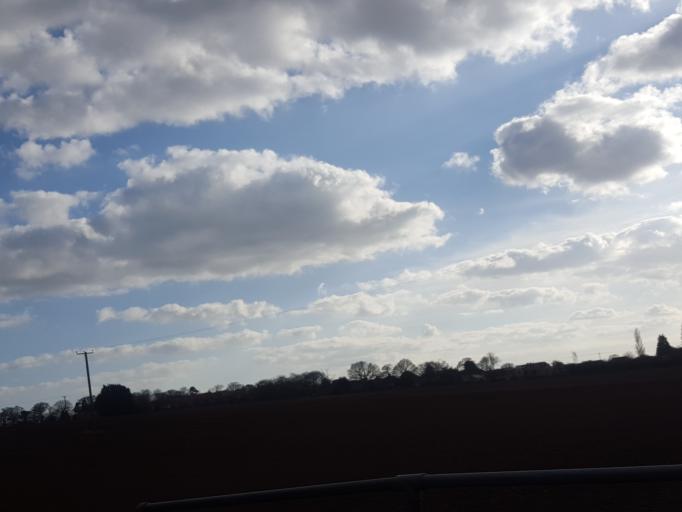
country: GB
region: England
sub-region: Essex
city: Little Clacton
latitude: 51.8535
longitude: 1.1230
